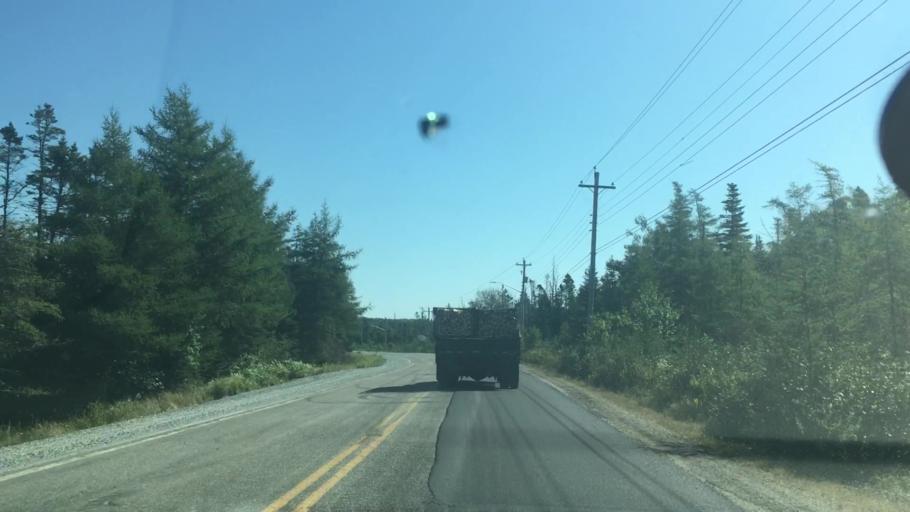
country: CA
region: Nova Scotia
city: New Glasgow
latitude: 44.9035
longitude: -62.4587
